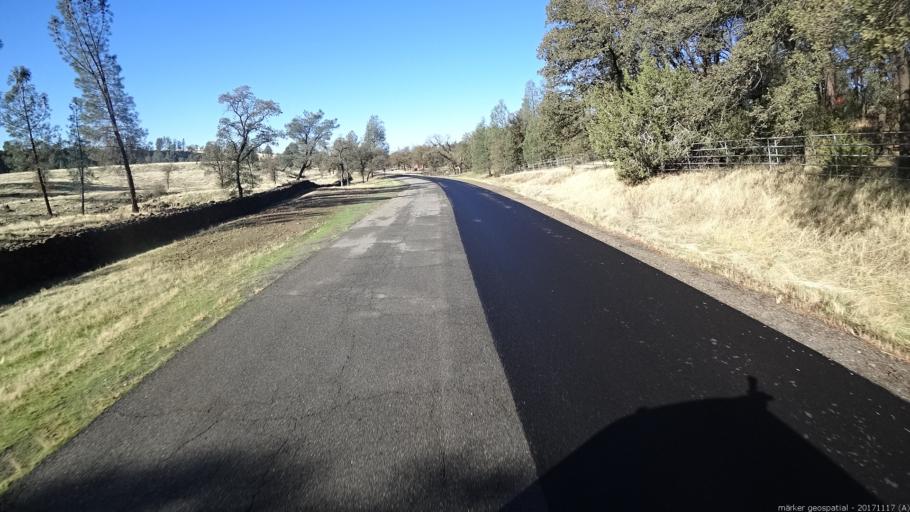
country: US
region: California
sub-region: Shasta County
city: Cottonwood
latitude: 40.4399
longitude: -122.1314
